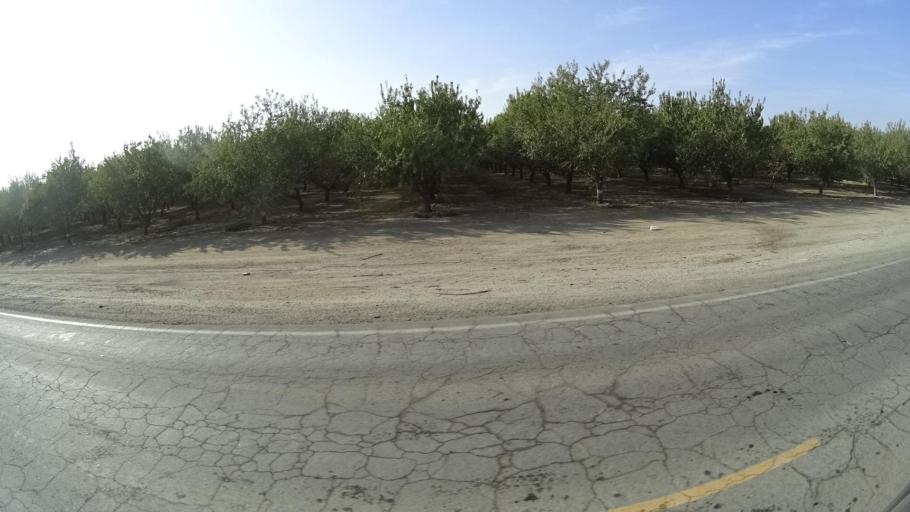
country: US
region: California
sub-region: Kern County
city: Delano
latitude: 35.7522
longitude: -119.2233
